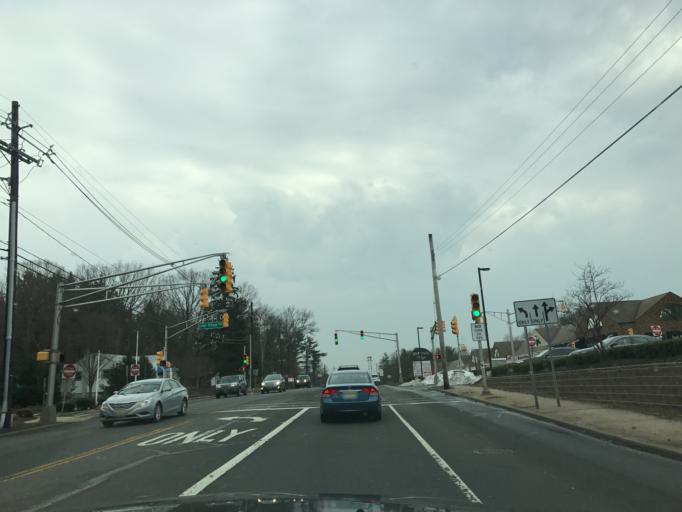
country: US
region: New Jersey
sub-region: Middlesex County
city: Milltown
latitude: 40.4525
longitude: -74.4245
